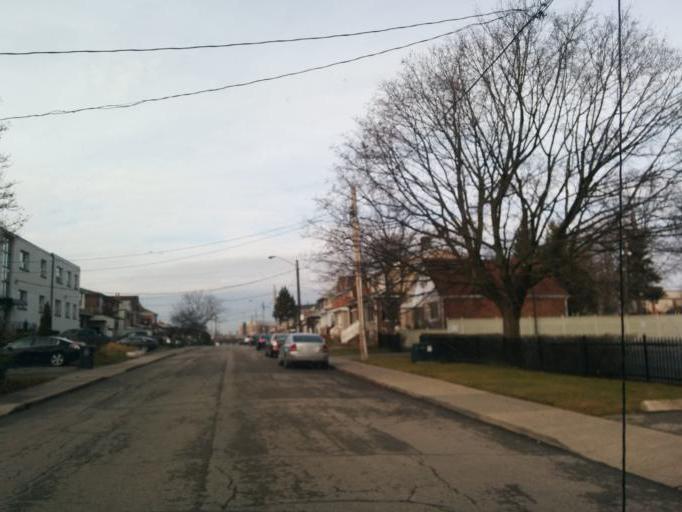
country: CA
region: Ontario
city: Etobicoke
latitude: 43.5996
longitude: -79.5130
